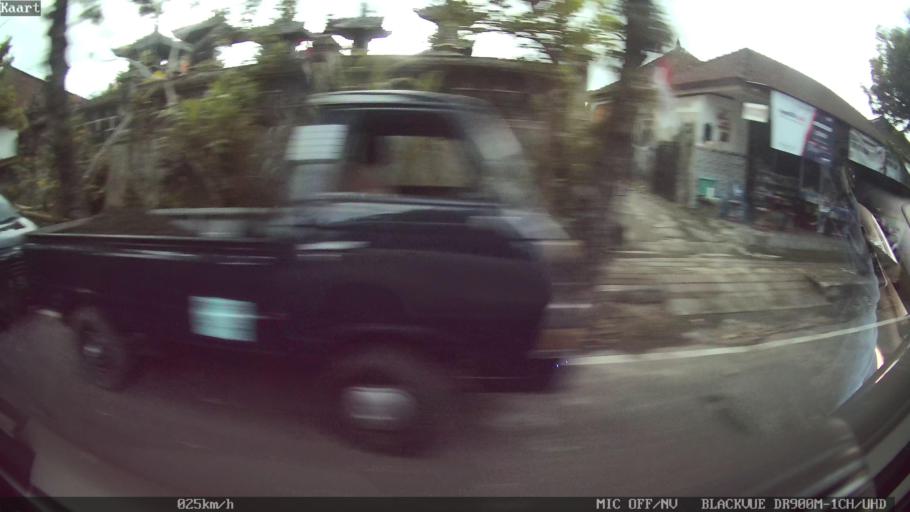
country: ID
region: Bali
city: Banjar Jambe Baleran
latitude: -8.5355
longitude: 115.1233
